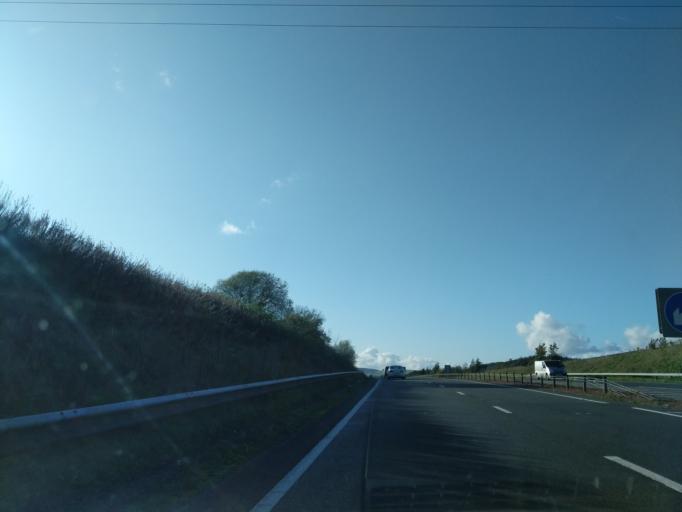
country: GB
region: Scotland
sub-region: Dumfries and Galloway
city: Dumfries
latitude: 55.0593
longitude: -3.6867
